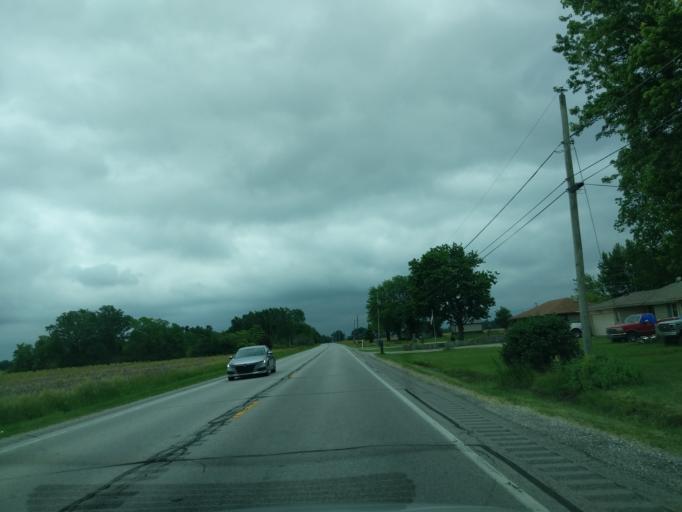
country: US
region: Indiana
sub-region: Madison County
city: Frankton
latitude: 40.2775
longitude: -85.7495
